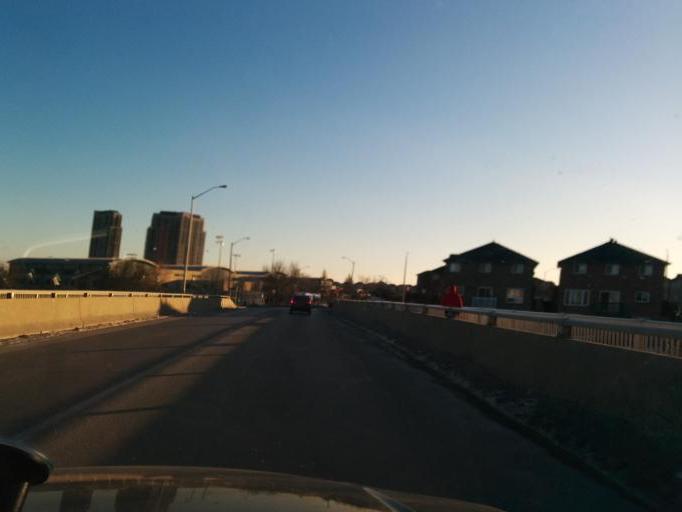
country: CA
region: Ontario
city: Etobicoke
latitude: 43.7313
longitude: -79.6198
